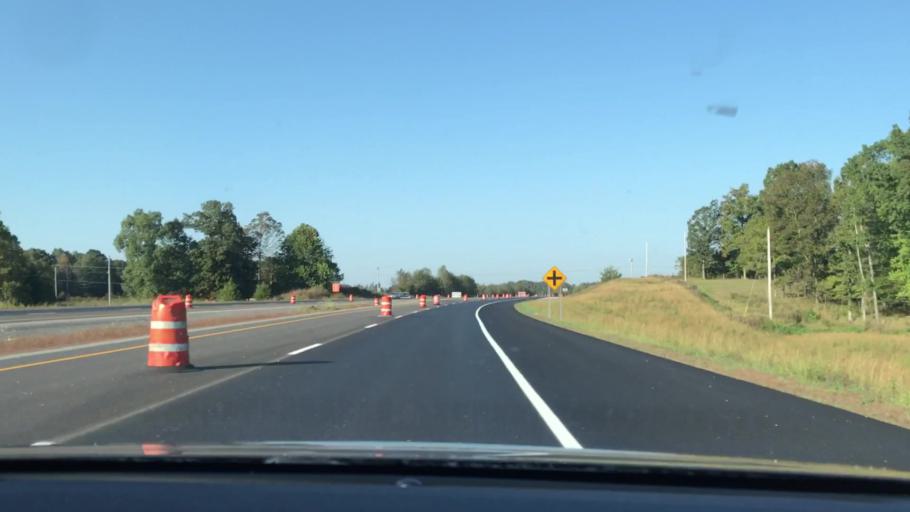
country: US
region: Kentucky
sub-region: Trigg County
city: Cadiz
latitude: 36.8398
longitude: -87.8403
